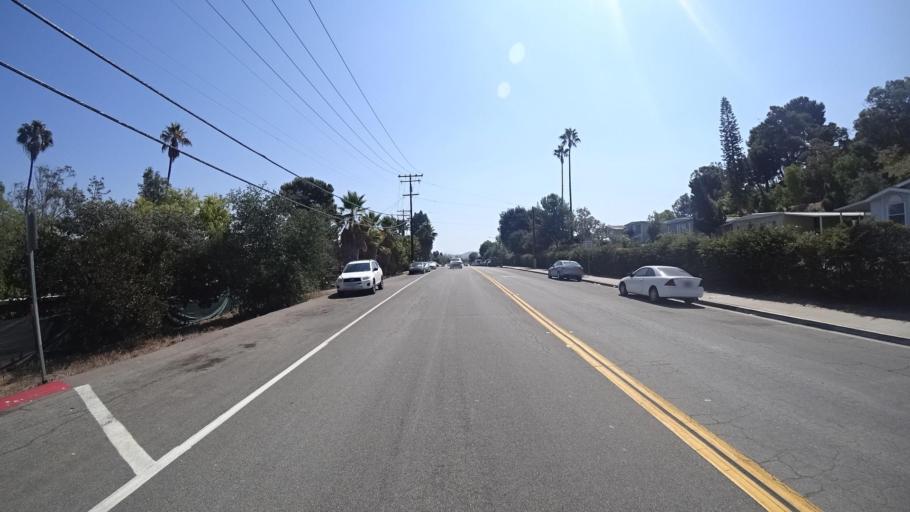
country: US
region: California
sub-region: San Diego County
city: Lake San Marcos
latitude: 33.1504
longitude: -117.2028
